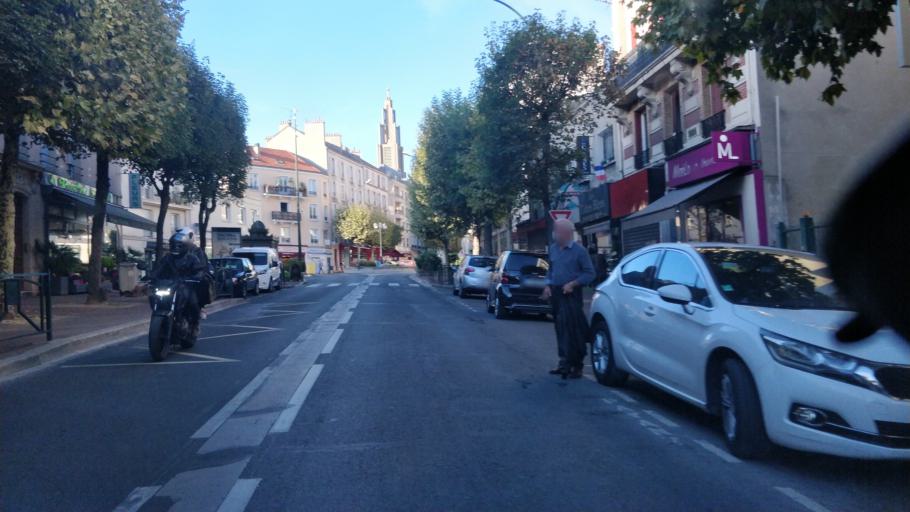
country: FR
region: Ile-de-France
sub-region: Departement de Seine-Saint-Denis
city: Le Raincy
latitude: 48.8941
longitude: 2.5133
